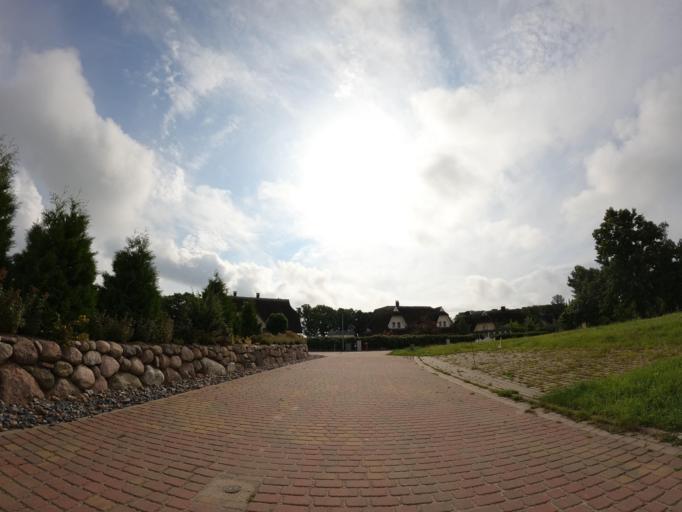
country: DE
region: Mecklenburg-Vorpommern
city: Ostseebad Gohren
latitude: 54.3221
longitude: 13.7279
